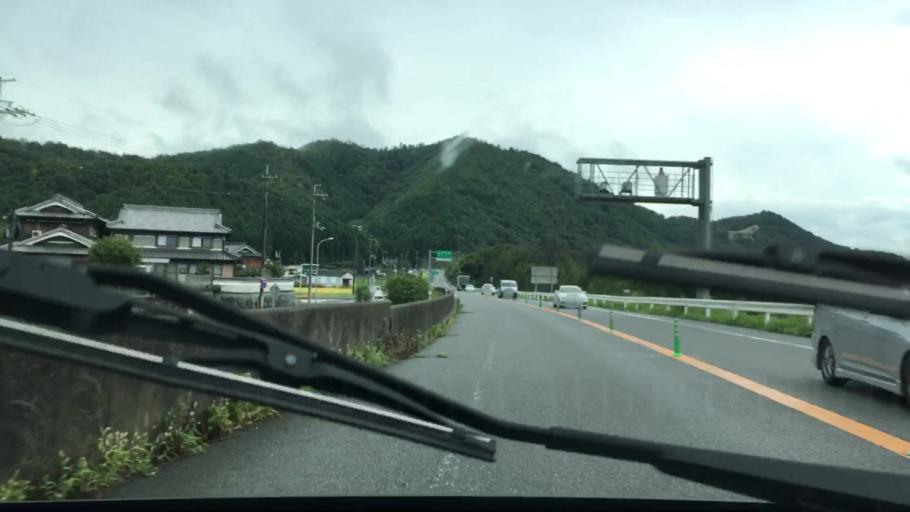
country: JP
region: Hyogo
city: Himeji
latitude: 35.0064
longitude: 134.7648
